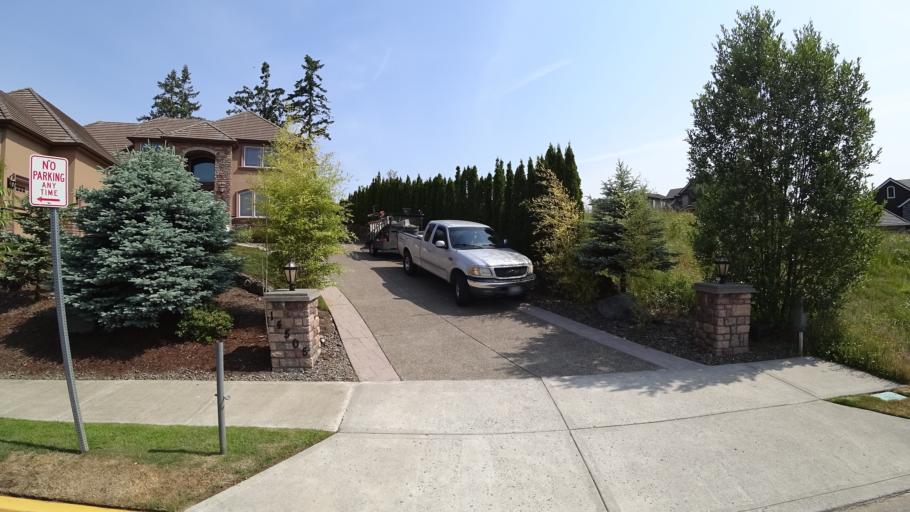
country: US
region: Oregon
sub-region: Clackamas County
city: Happy Valley
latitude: 45.4587
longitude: -122.5138
